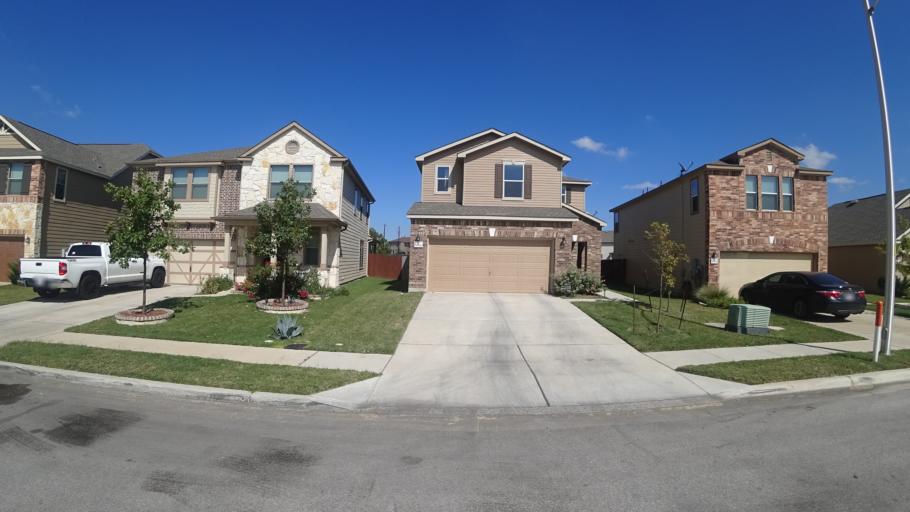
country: US
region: Texas
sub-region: Travis County
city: Manor
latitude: 30.3483
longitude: -97.6189
